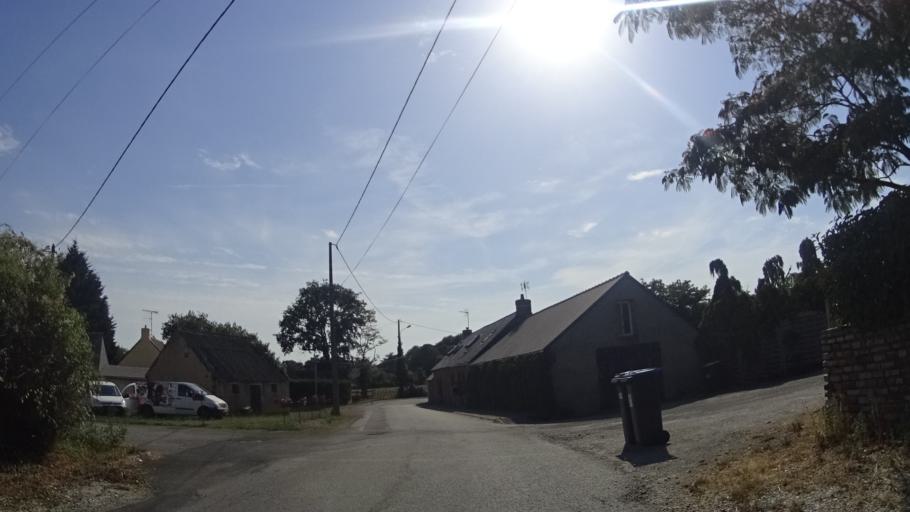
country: FR
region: Pays de la Loire
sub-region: Departement de la Loire-Atlantique
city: Donges
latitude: 47.3205
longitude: -2.0603
